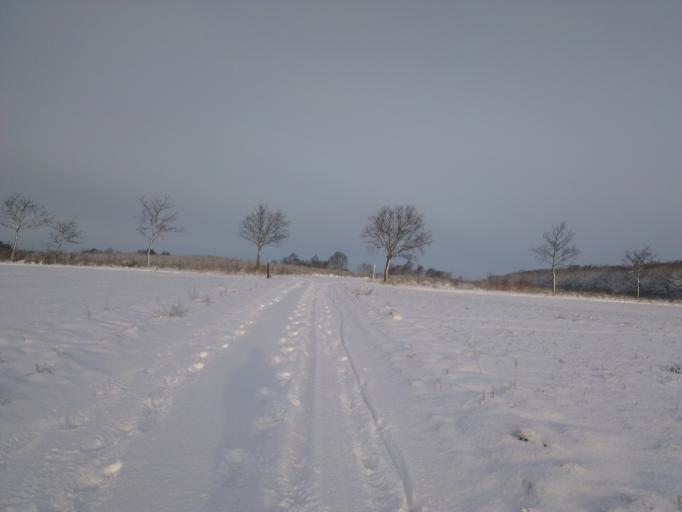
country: DK
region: Capital Region
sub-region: Frederikssund Kommune
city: Jaegerspris
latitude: 55.8529
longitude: 11.9648
